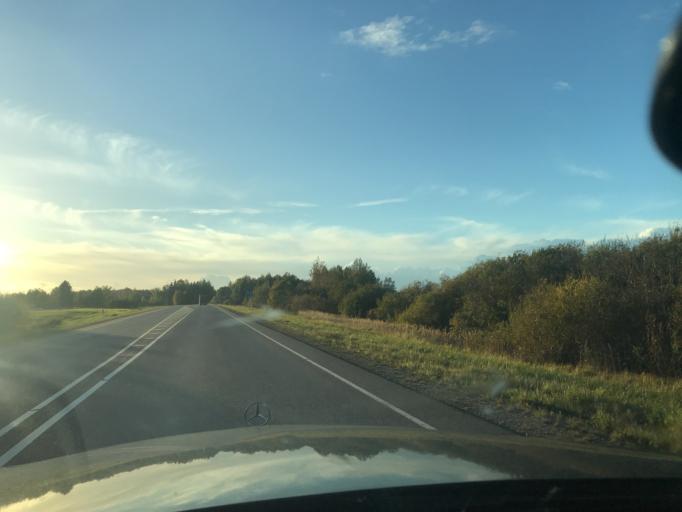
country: EE
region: Vorumaa
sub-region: Voru linn
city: Voru
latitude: 57.8605
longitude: 26.9919
